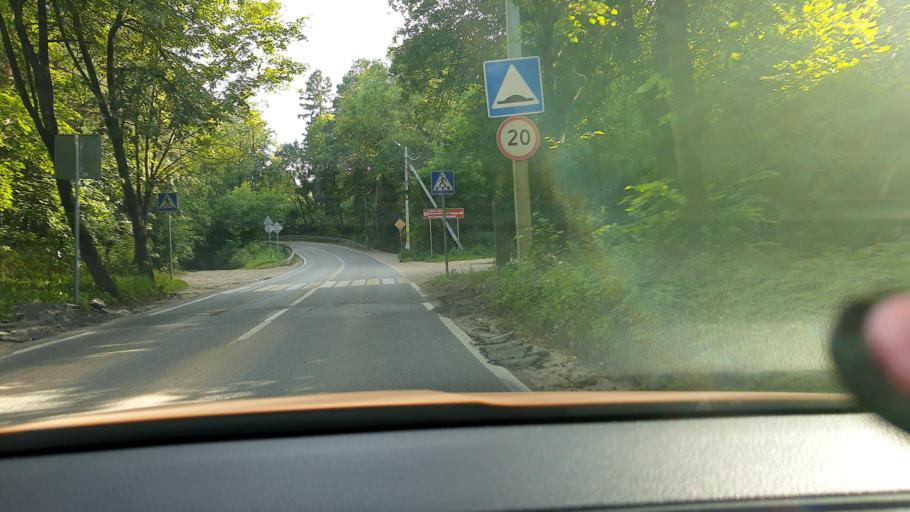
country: RU
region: Moskovskaya
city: Zvenigorod
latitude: 55.7356
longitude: 36.8467
